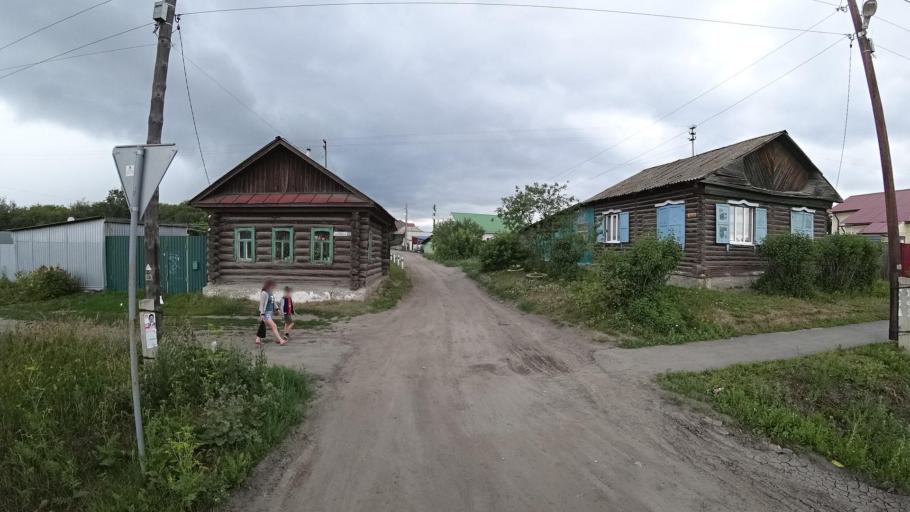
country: RU
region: Sverdlovsk
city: Kamyshlov
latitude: 56.8470
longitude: 62.6758
